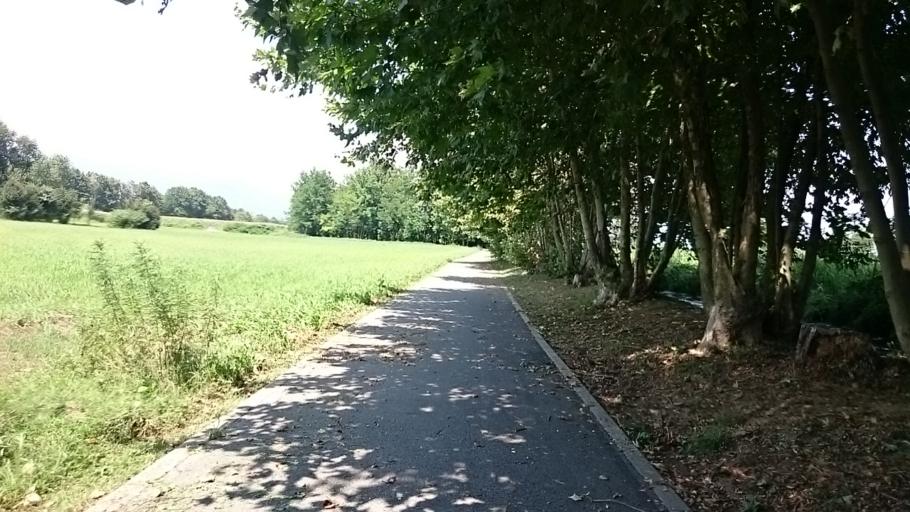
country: IT
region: Veneto
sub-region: Provincia di Vicenza
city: Rosa
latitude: 45.7126
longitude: 11.7371
